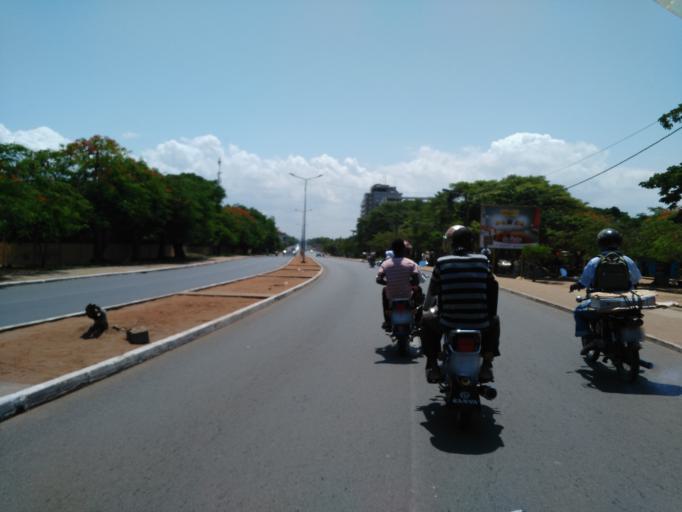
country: TG
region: Maritime
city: Lome
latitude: 6.1513
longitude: 1.2301
